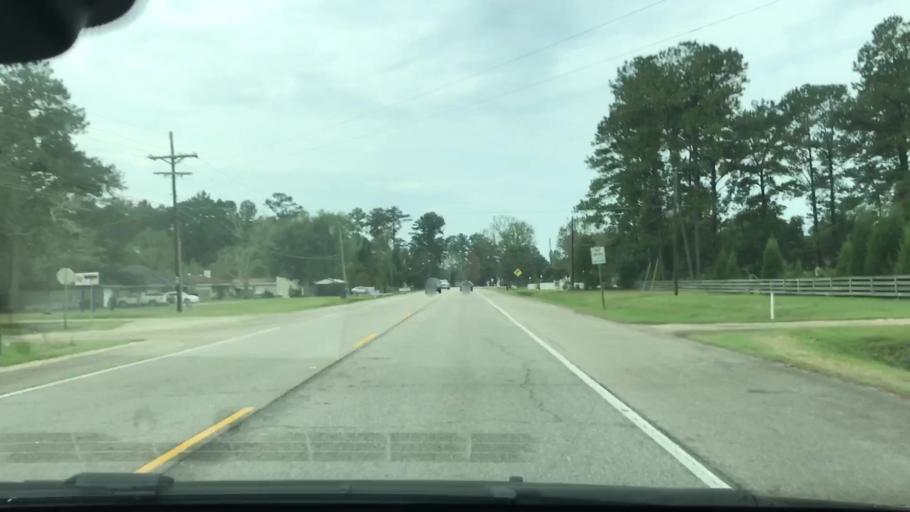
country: US
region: Louisiana
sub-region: Saint Tammany Parish
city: Pearl River
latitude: 30.3870
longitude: -89.7637
